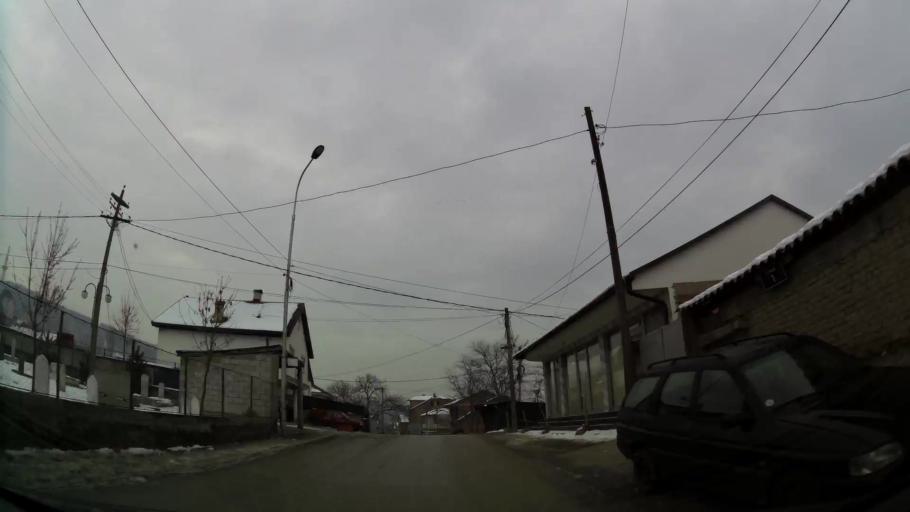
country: MK
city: Kondovo
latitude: 42.0111
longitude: 21.3125
